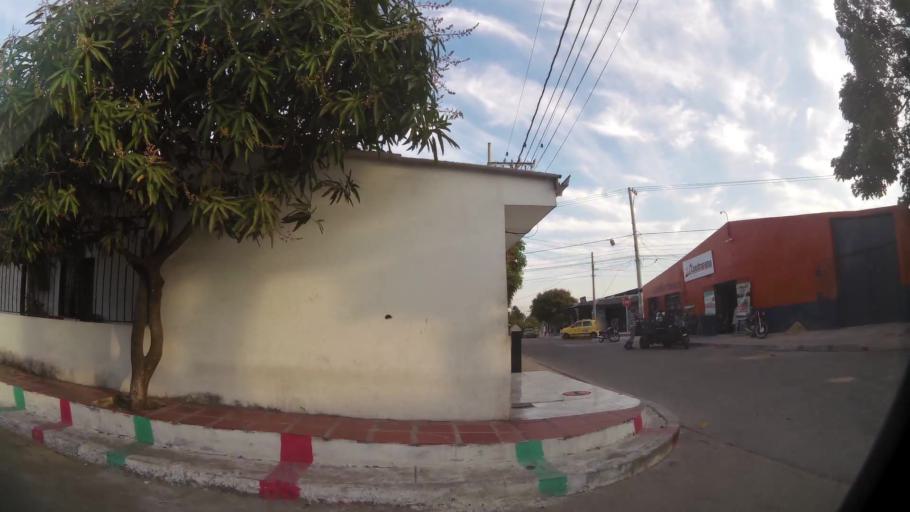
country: CO
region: Atlantico
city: Barranquilla
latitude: 10.9584
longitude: -74.8262
